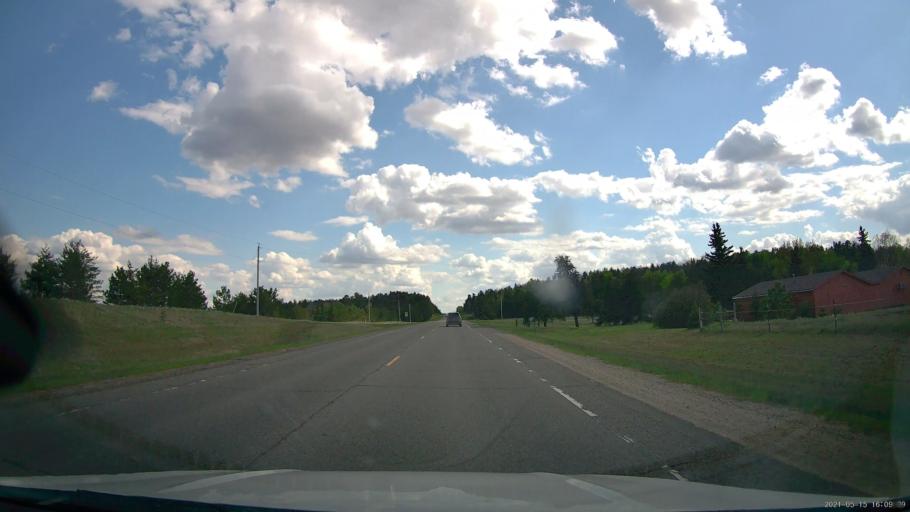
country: US
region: Minnesota
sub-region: Hubbard County
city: Park Rapids
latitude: 46.9487
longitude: -94.9528
